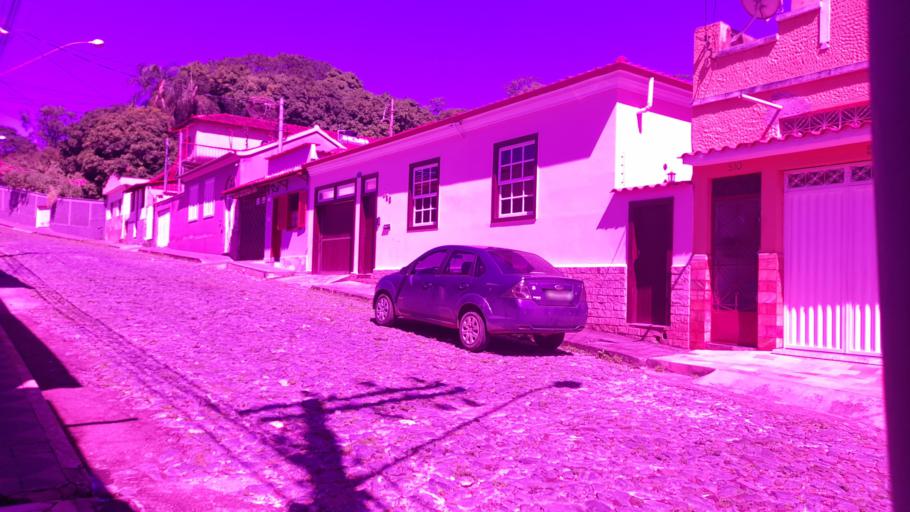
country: BR
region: Minas Gerais
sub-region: Sao Joao Del Rei
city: Sao Joao del Rei
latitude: -21.1375
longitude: -44.2678
